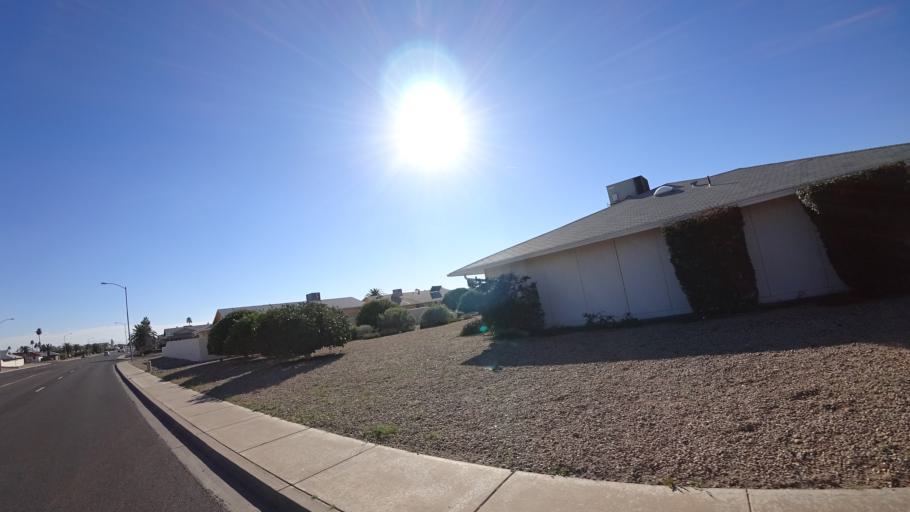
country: US
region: Arizona
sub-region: Maricopa County
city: Sun City West
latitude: 33.6649
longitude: -112.3315
